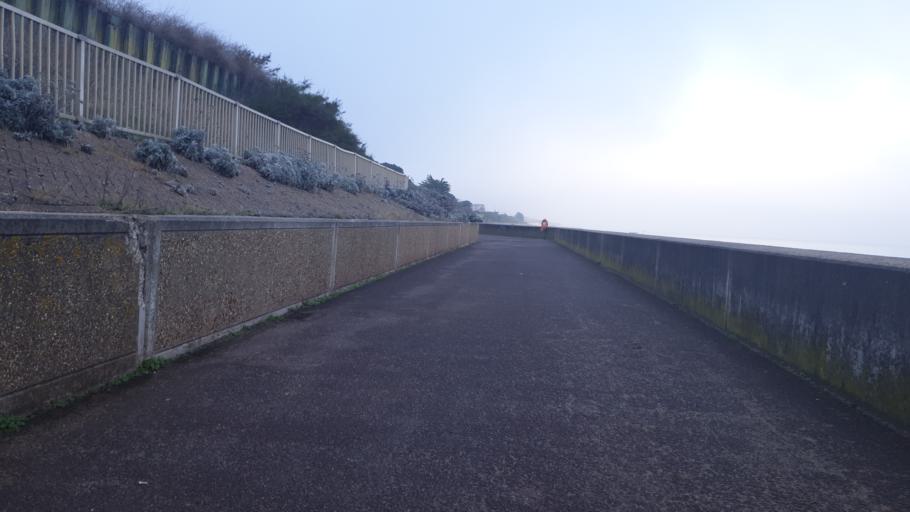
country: GB
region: England
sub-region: Essex
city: Clacton-on-Sea
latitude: 51.7897
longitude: 1.1615
